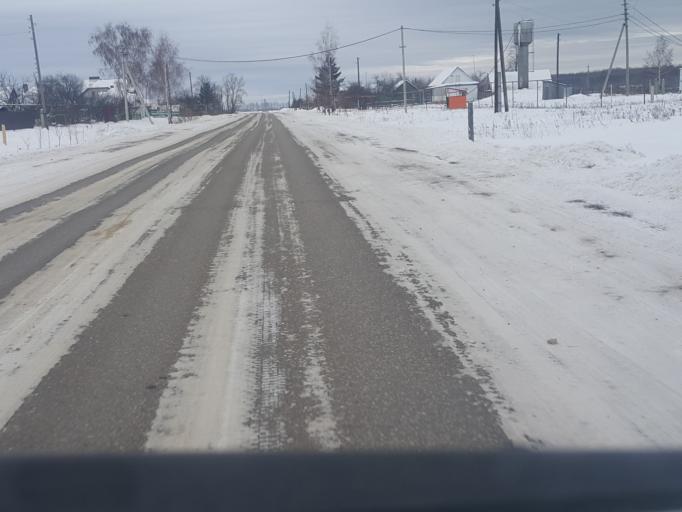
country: RU
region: Tambov
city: Platonovka
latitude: 52.8321
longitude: 41.8091
